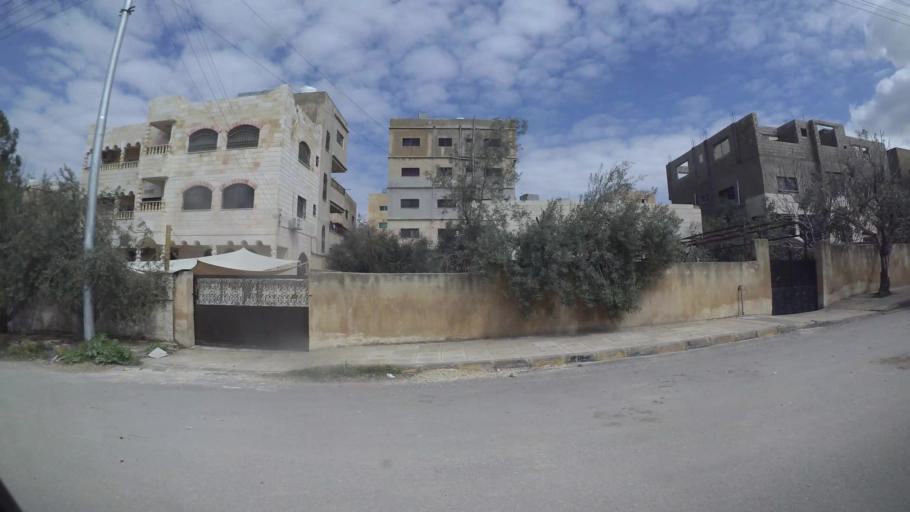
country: JO
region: Amman
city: Al Jubayhah
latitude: 32.0636
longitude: 35.8314
